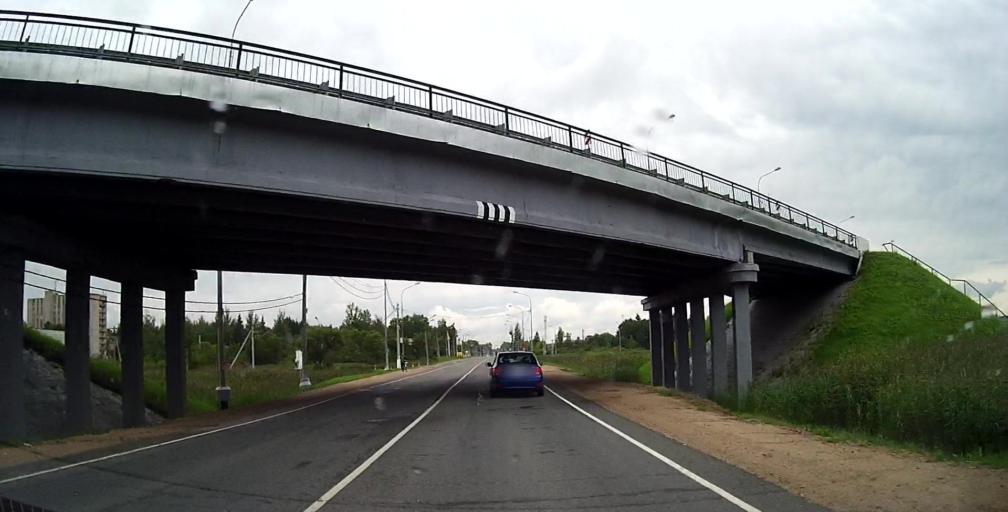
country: RU
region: Smolensk
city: Katyn'
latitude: 54.7784
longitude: 31.8003
